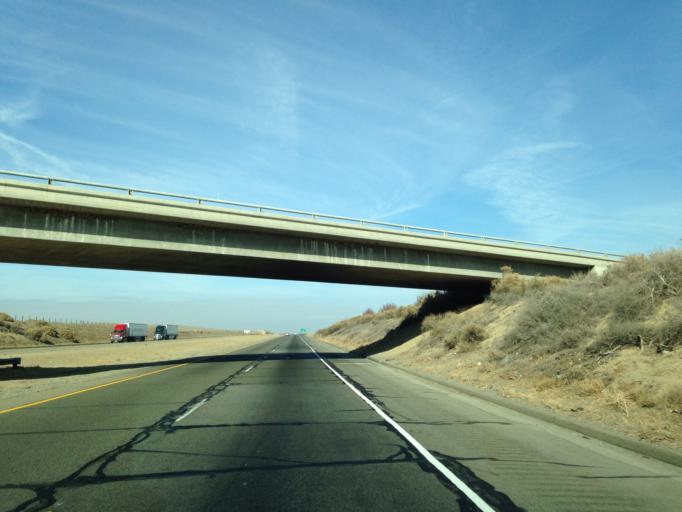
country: US
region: California
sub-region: Kings County
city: Kettleman City
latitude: 35.9587
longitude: -119.9365
